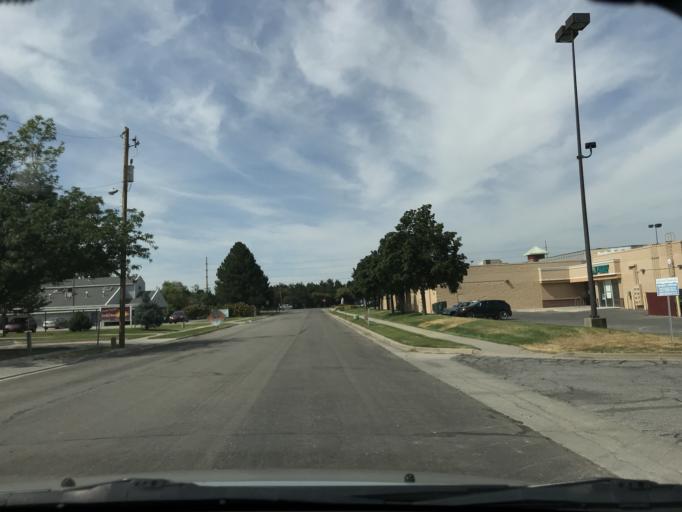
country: US
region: Utah
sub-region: Salt Lake County
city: Taylorsville
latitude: 40.6659
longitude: -111.9433
